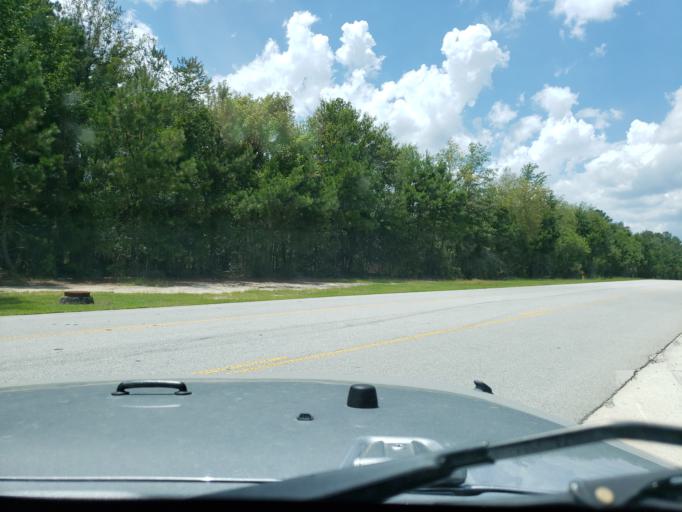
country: US
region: Georgia
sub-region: Chatham County
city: Bloomingdale
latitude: 32.1095
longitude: -81.2792
